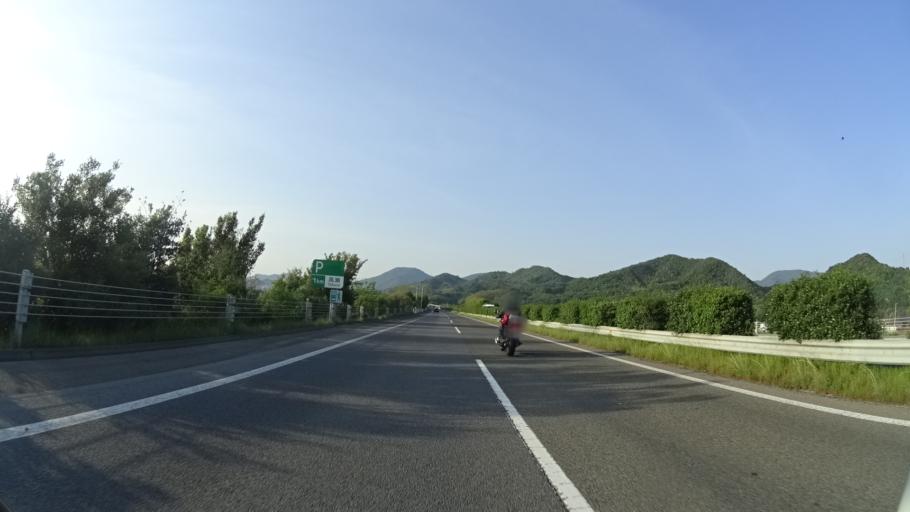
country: JP
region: Kagawa
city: Kan'onjicho
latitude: 34.1700
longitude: 133.7328
